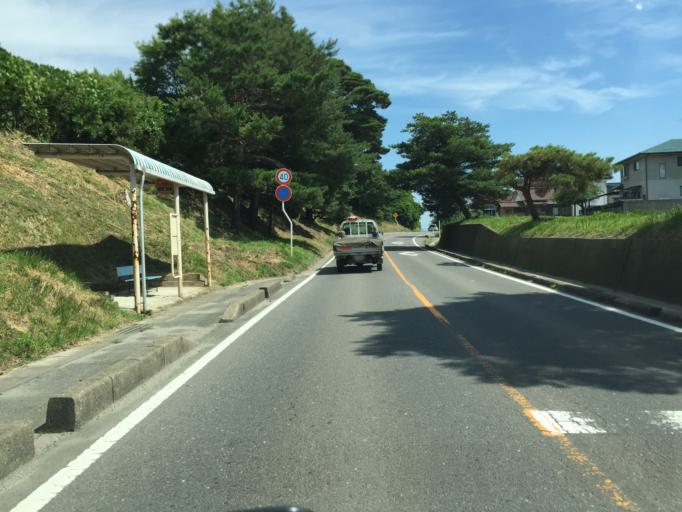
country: JP
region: Fukushima
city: Koriyama
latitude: 37.4328
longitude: 140.3911
